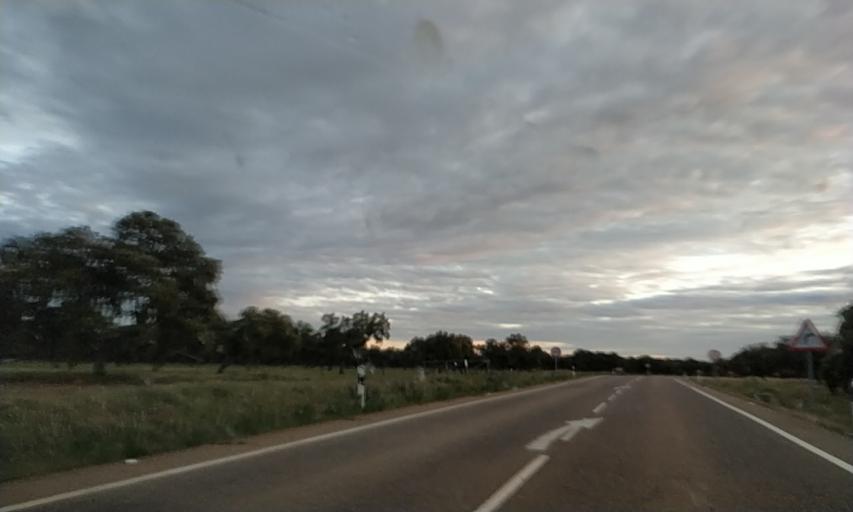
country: ES
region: Extremadura
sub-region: Provincia de Badajoz
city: Villar del Rey
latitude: 39.0421
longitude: -6.8091
